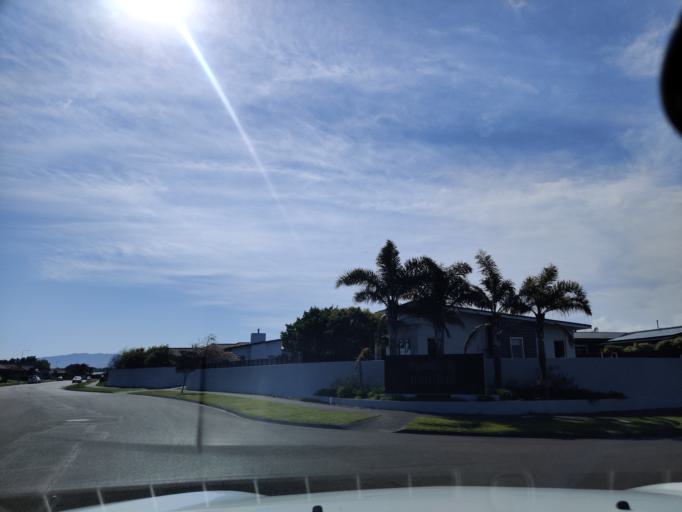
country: NZ
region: Manawatu-Wanganui
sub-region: Palmerston North City
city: Palmerston North
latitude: -40.3332
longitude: 175.6571
